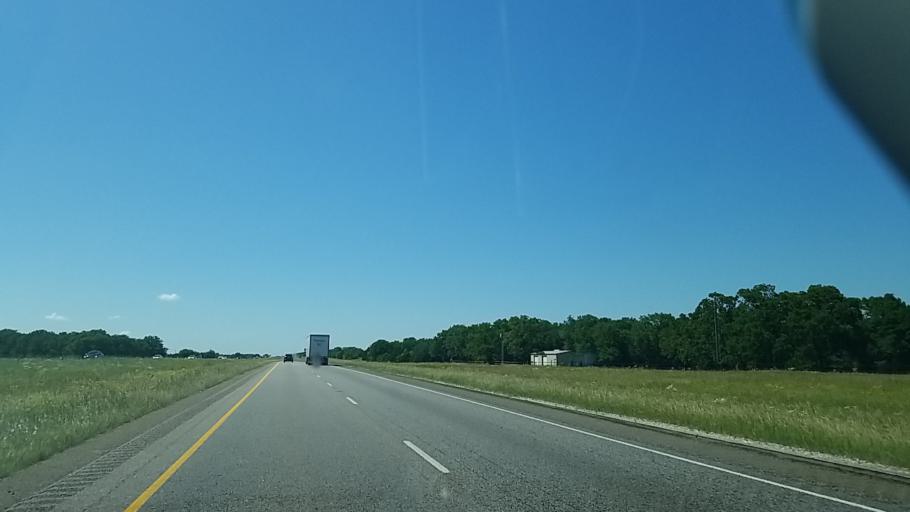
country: US
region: Texas
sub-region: Freestone County
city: Fairfield
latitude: 31.7631
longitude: -96.2120
